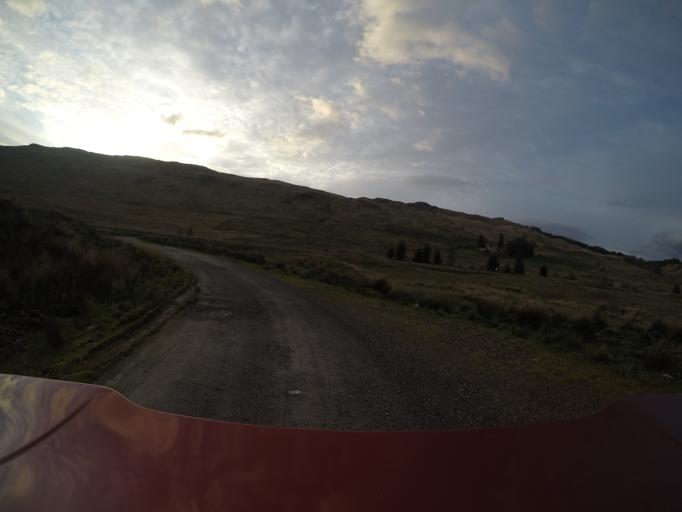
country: GB
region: Scotland
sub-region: Argyll and Bute
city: Garelochhead
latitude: 56.3796
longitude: -4.6399
